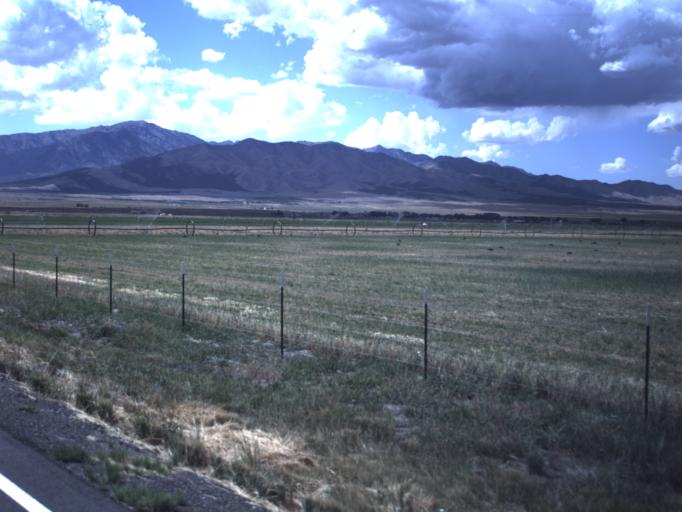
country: US
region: Utah
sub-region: Tooele County
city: Tooele
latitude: 40.3369
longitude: -112.4279
